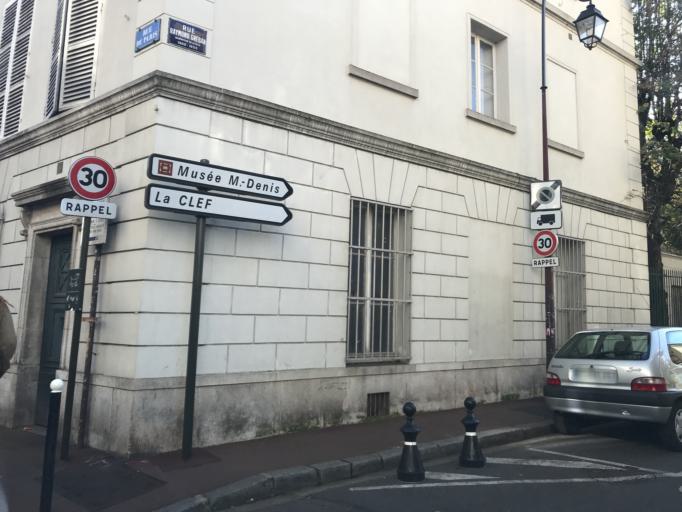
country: FR
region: Ile-de-France
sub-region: Departement des Yvelines
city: Le Pecq
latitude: 48.8953
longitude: 2.0937
